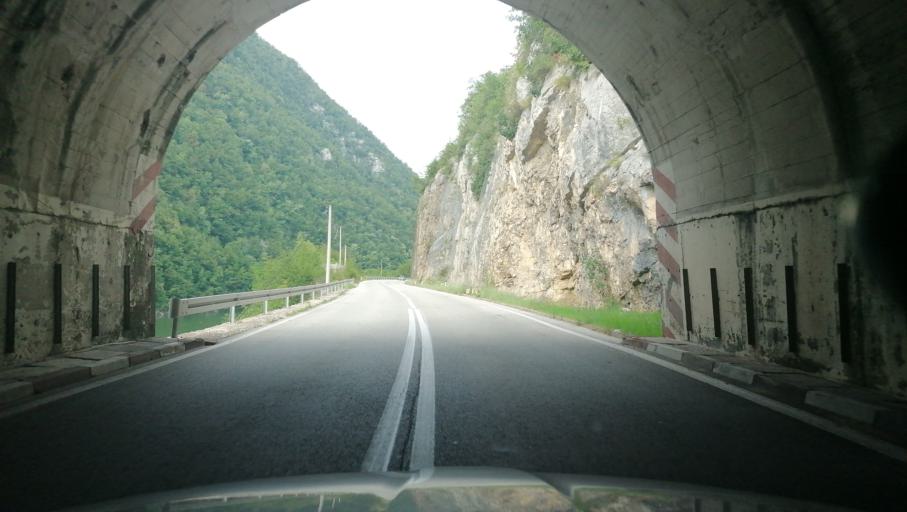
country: BA
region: Federation of Bosnia and Herzegovina
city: Jajce
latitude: 44.4652
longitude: 17.2111
